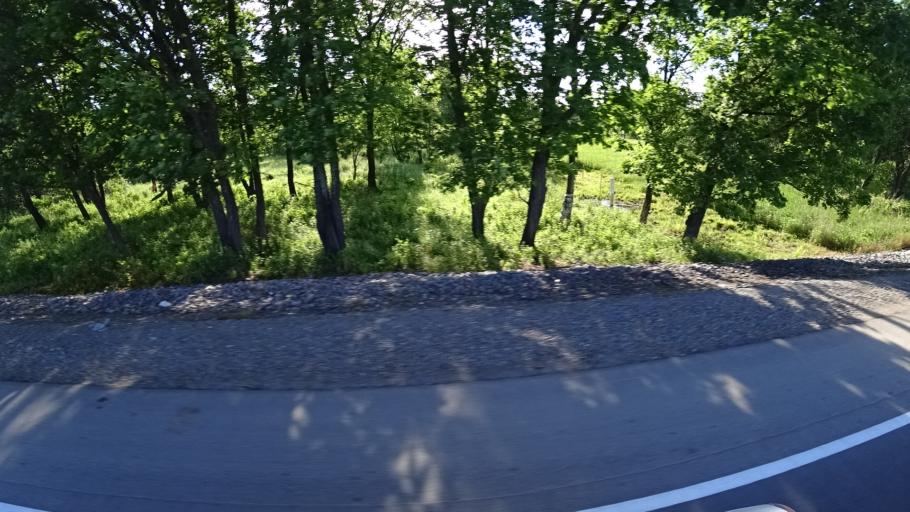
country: RU
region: Khabarovsk Krai
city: Khor
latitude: 47.8576
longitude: 134.9623
